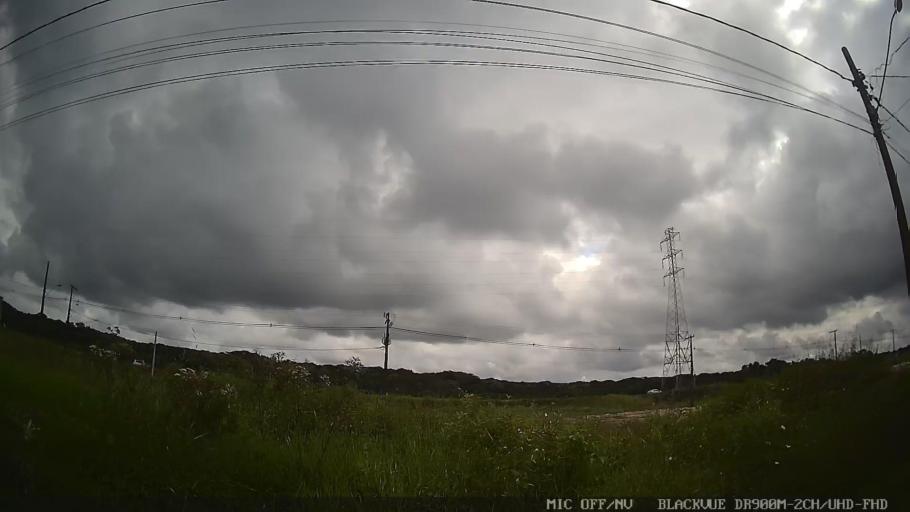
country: BR
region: Sao Paulo
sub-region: Itanhaem
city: Itanhaem
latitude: -24.2023
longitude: -46.8470
